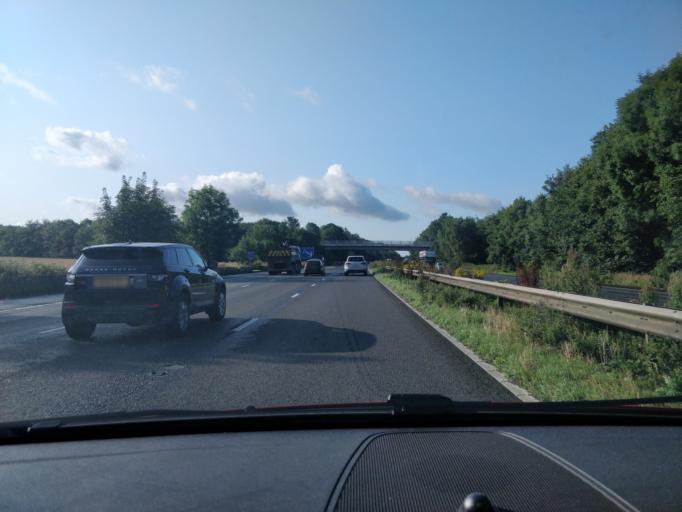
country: GB
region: England
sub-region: Knowsley
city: Knowsley
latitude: 53.4473
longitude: -2.8610
